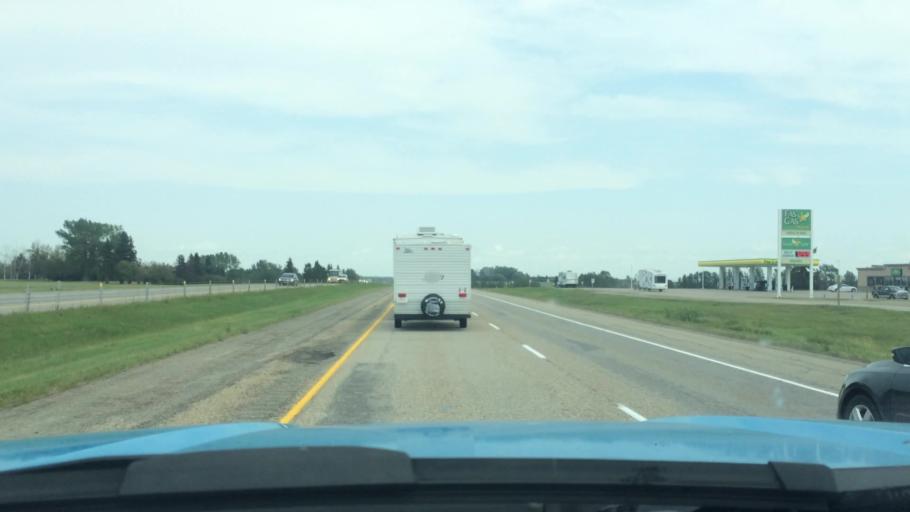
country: CA
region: Alberta
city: Olds
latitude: 51.9508
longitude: -114.0207
